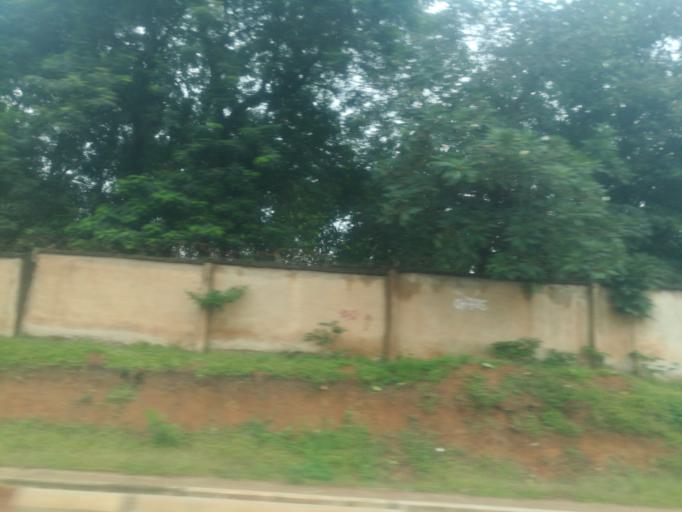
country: NG
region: Oyo
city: Ibadan
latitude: 7.3939
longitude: 3.9247
